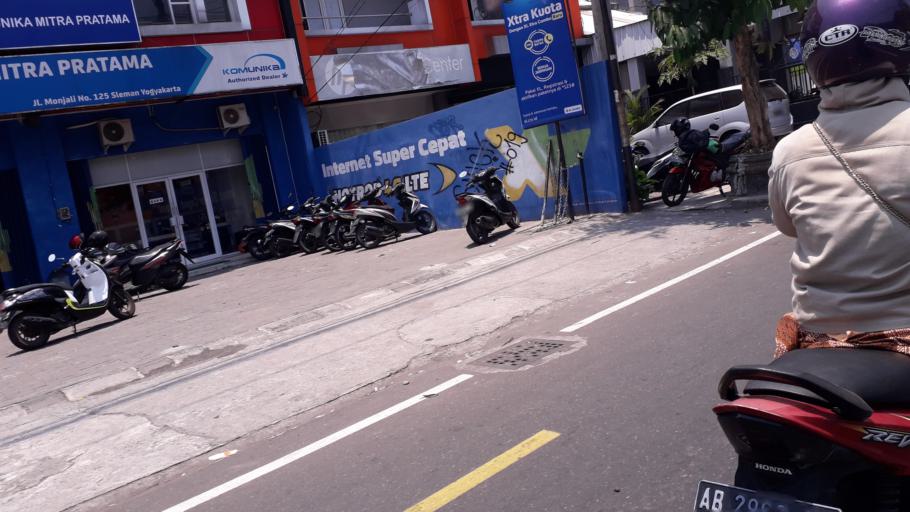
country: ID
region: Daerah Istimewa Yogyakarta
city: Yogyakarta
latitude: -7.7628
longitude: 110.3694
